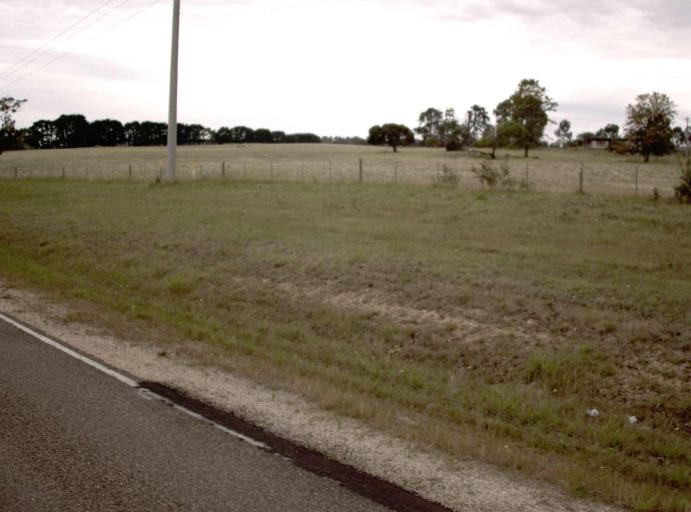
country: AU
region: Victoria
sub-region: Wellington
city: Sale
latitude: -38.1732
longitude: 147.1150
